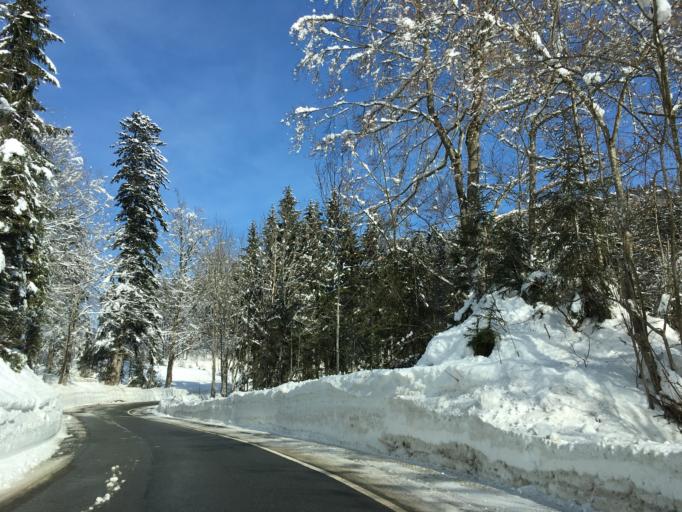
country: DE
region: Bavaria
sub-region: Upper Bavaria
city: Burg Unter-Falkenstein
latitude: 47.6740
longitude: 12.0843
